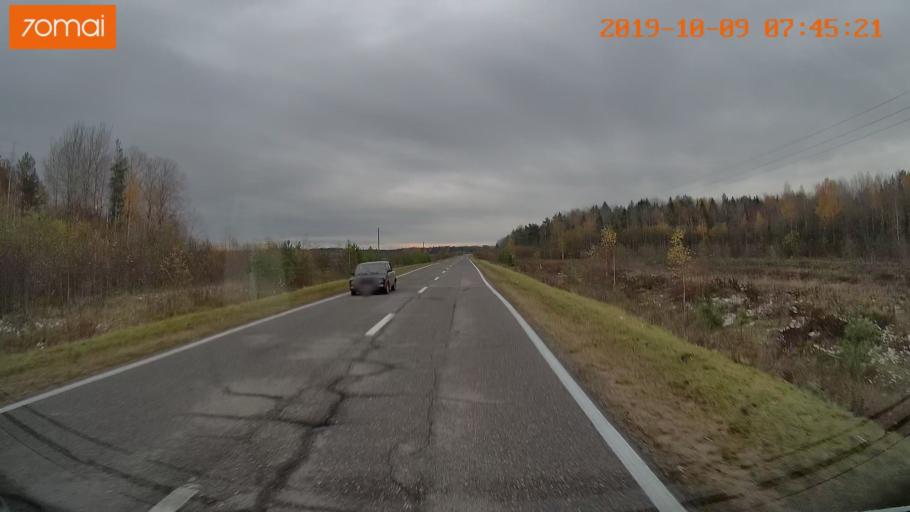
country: RU
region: Jaroslavl
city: Kukoboy
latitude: 58.6533
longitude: 39.7649
